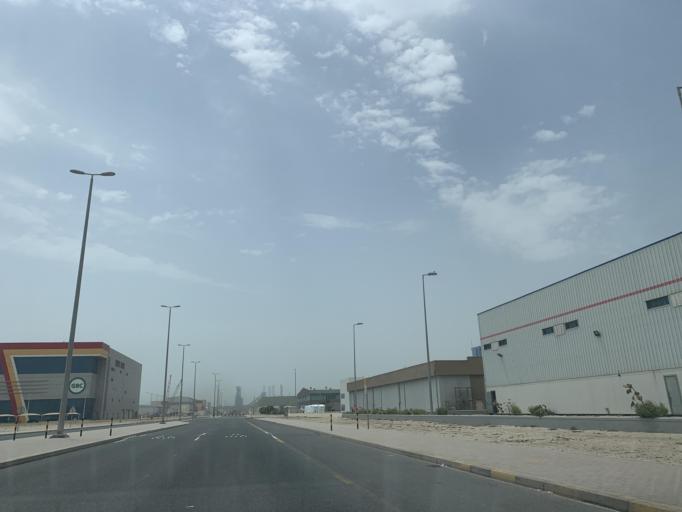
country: BH
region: Muharraq
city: Al Hadd
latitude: 26.2196
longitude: 50.6792
